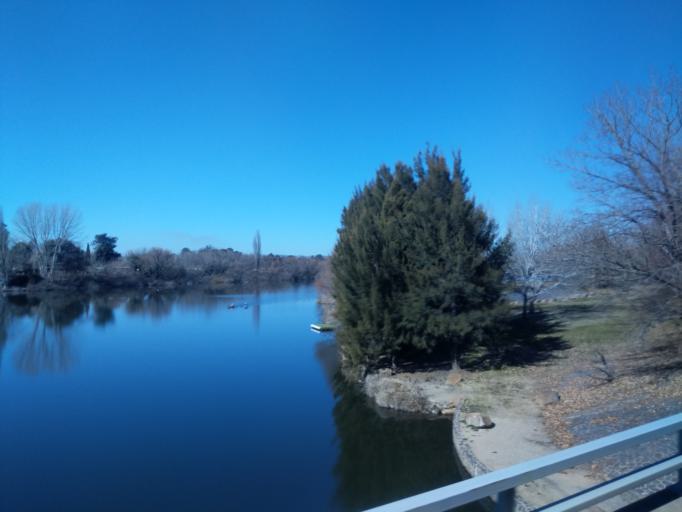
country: AU
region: Australian Capital Territory
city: Forrest
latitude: -35.3027
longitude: 149.1741
